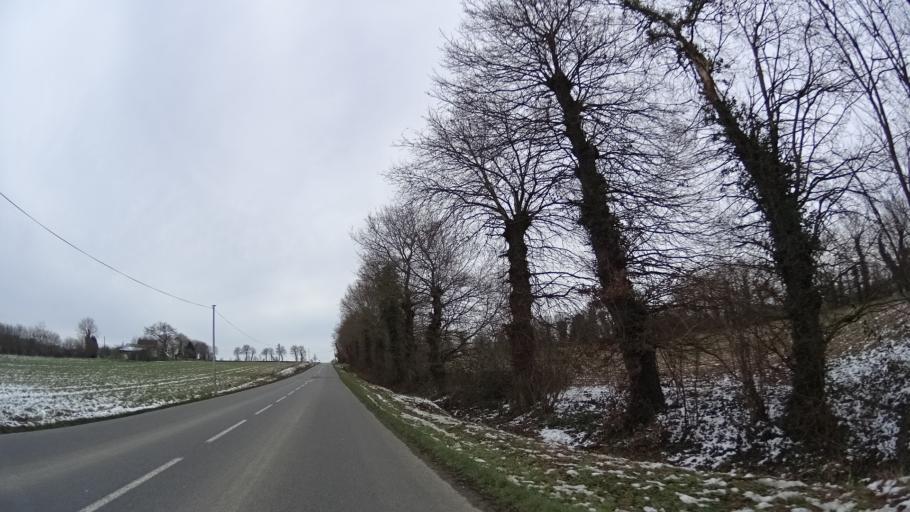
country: FR
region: Brittany
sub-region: Departement d'Ille-et-Vilaine
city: Irodouer
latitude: 48.2677
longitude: -1.9796
